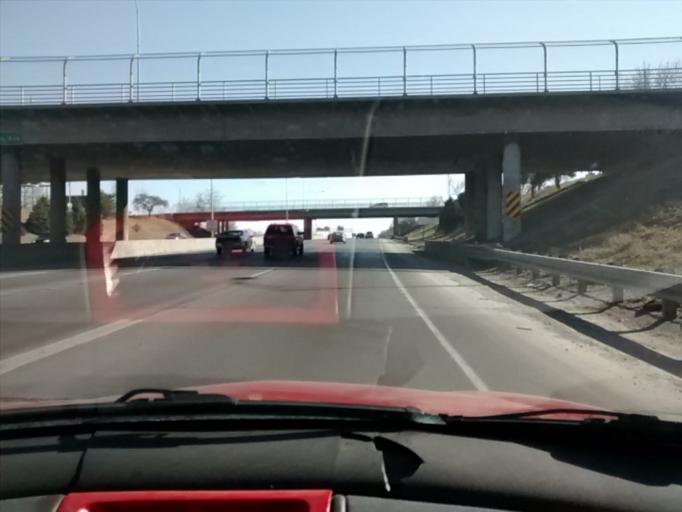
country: US
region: Nebraska
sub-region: Douglas County
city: Omaha
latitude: 41.2540
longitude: -95.9541
